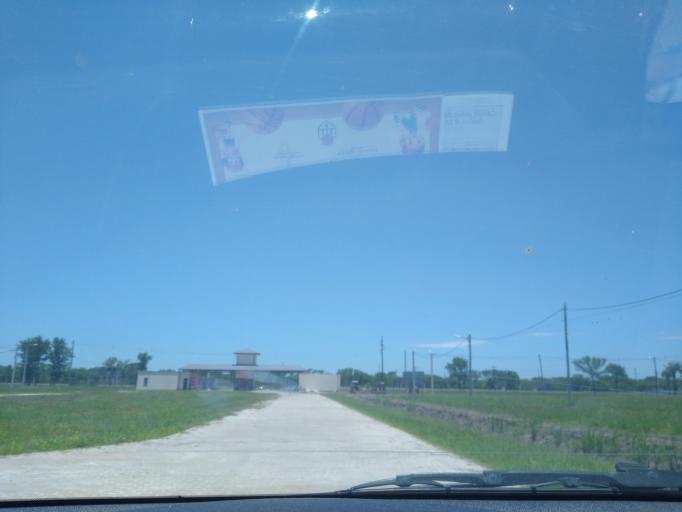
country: AR
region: Chaco
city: Makalle
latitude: -27.2509
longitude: -59.1635
